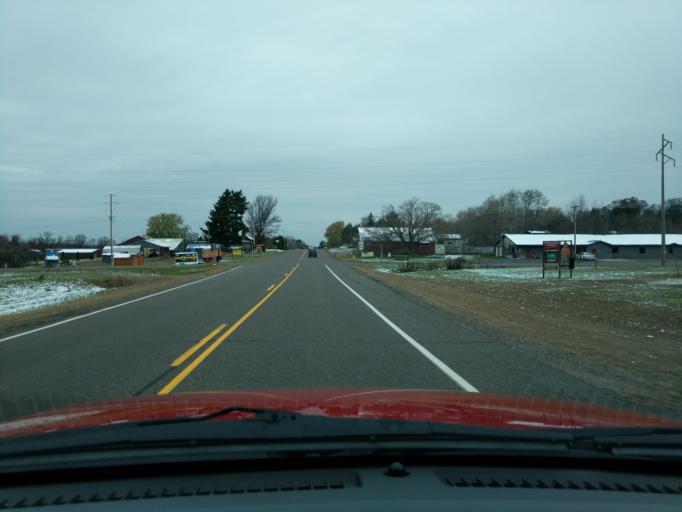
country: US
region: Wisconsin
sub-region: Burnett County
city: Siren
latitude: 45.8088
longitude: -92.1738
